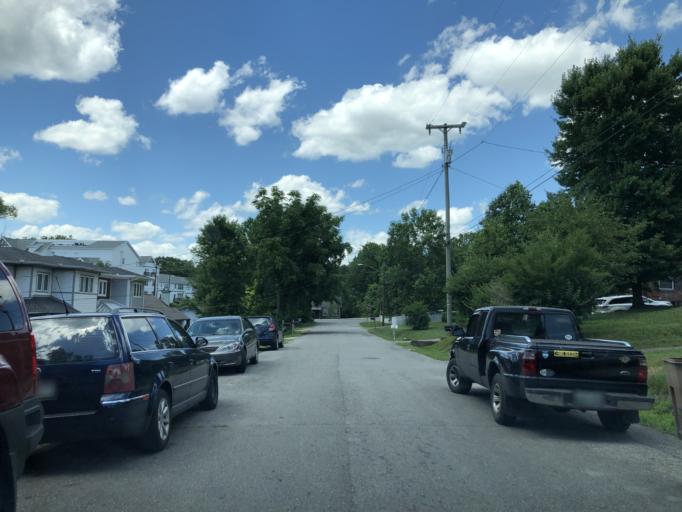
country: US
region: Tennessee
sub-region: Davidson County
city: Nashville
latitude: 36.1838
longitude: -86.7303
